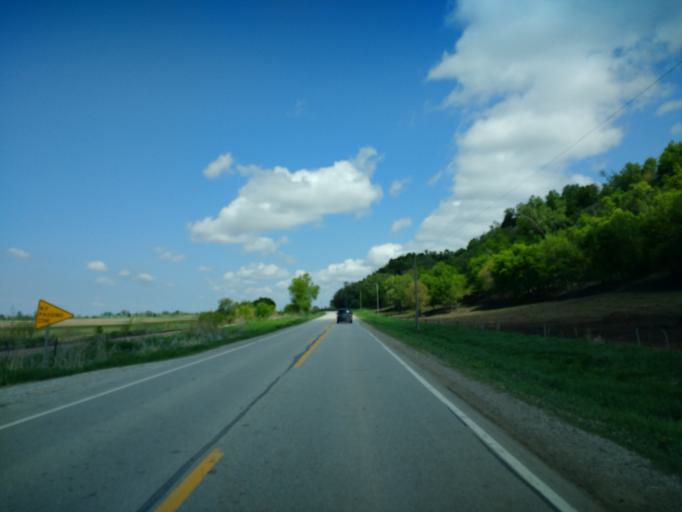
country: US
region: Iowa
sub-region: Harrison County
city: Missouri Valley
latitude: 41.4820
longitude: -95.8844
